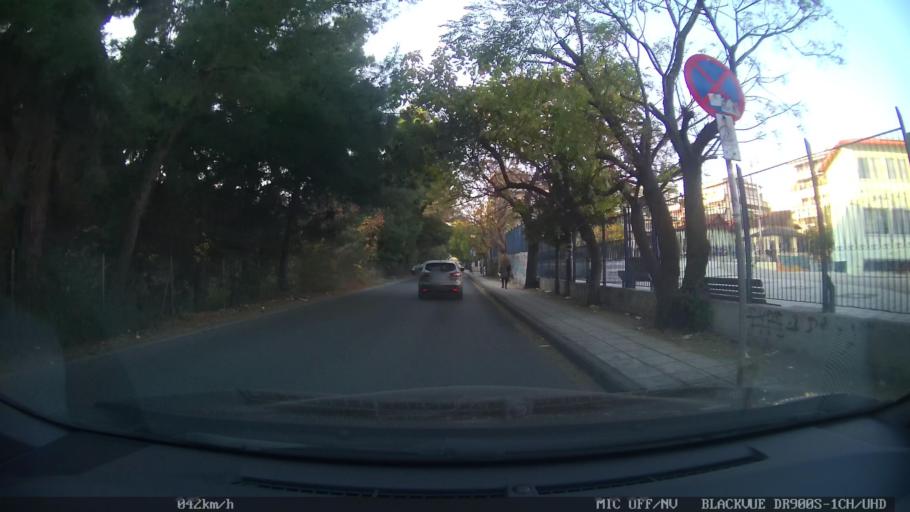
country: GR
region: Central Macedonia
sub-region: Nomos Thessalonikis
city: Triandria
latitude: 40.6092
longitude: 22.9819
